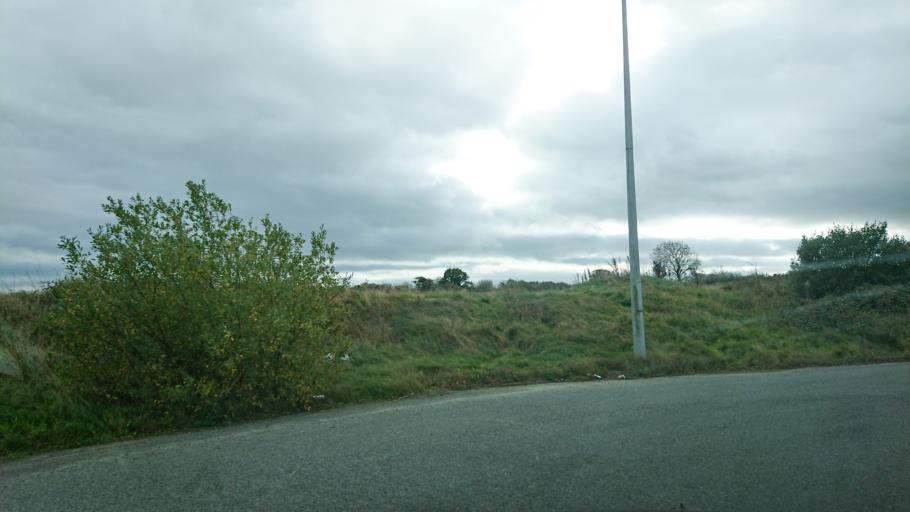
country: IE
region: Munster
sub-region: Waterford
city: Waterford
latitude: 52.2316
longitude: -7.1394
